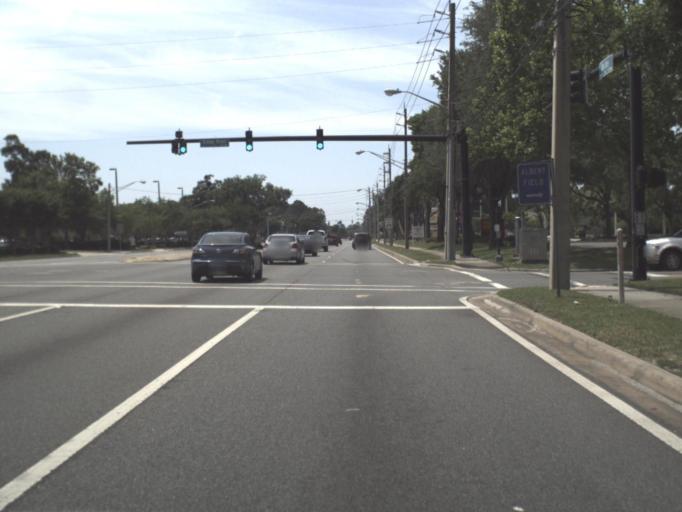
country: US
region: Florida
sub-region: Saint Johns County
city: Fruit Cove
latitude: 30.1500
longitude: -81.6327
